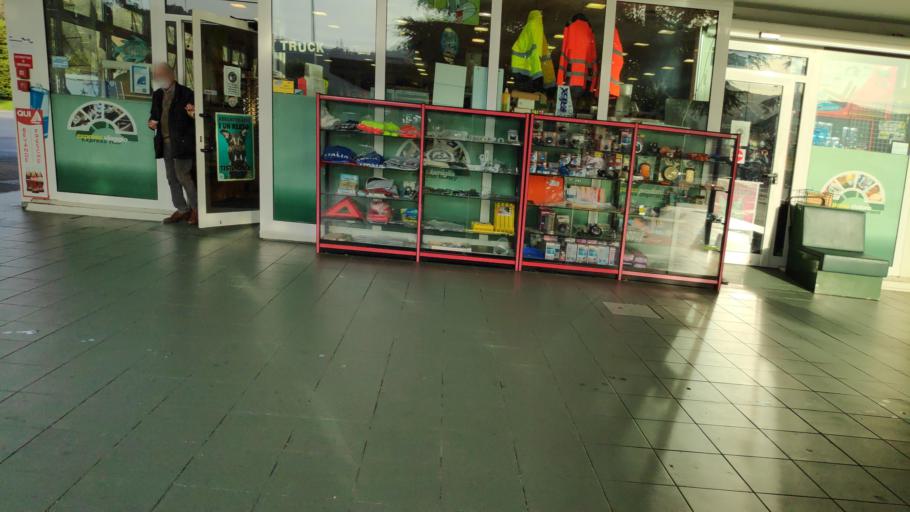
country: IT
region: Liguria
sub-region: Provincia di Savona
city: Vezzi Portio
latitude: 44.2253
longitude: 8.3602
